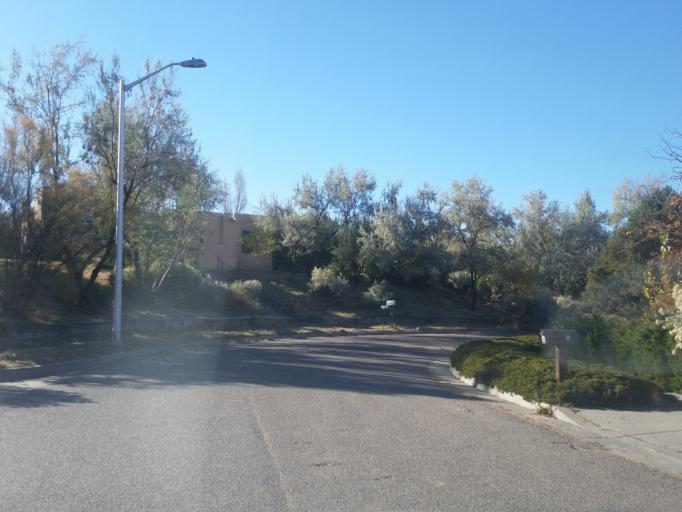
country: US
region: New Mexico
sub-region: Santa Fe County
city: Santa Fe
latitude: 35.6503
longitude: -105.9280
